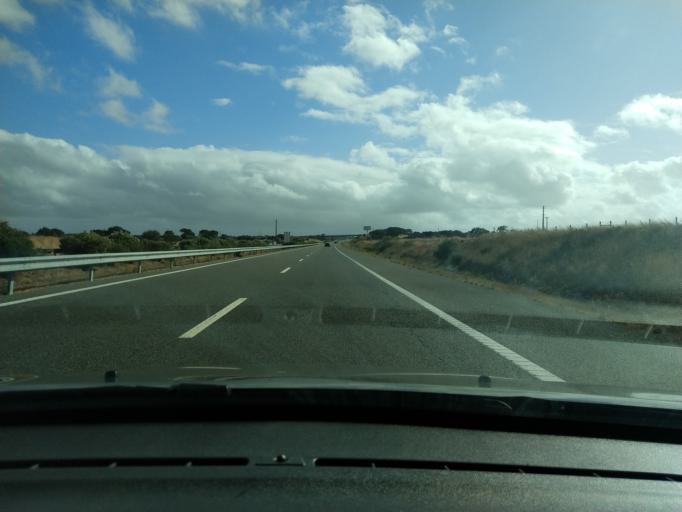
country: PT
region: Beja
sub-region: Ourique
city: Ourique
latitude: 37.6551
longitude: -8.1561
